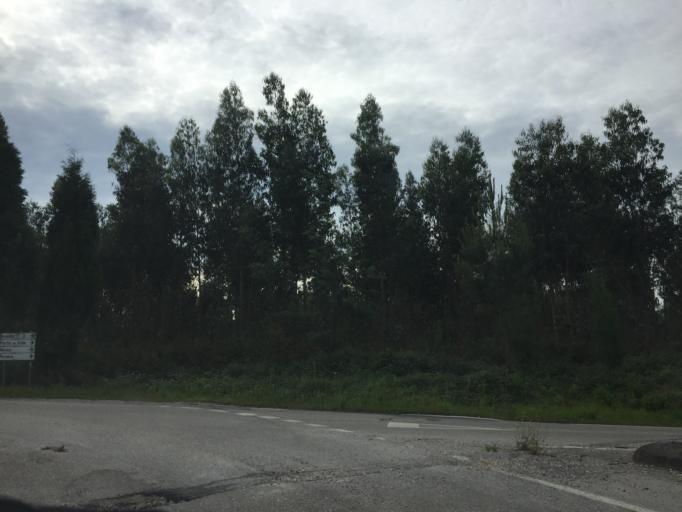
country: PT
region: Aveiro
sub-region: Anadia
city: Arcos
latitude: 40.4805
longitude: -8.4309
